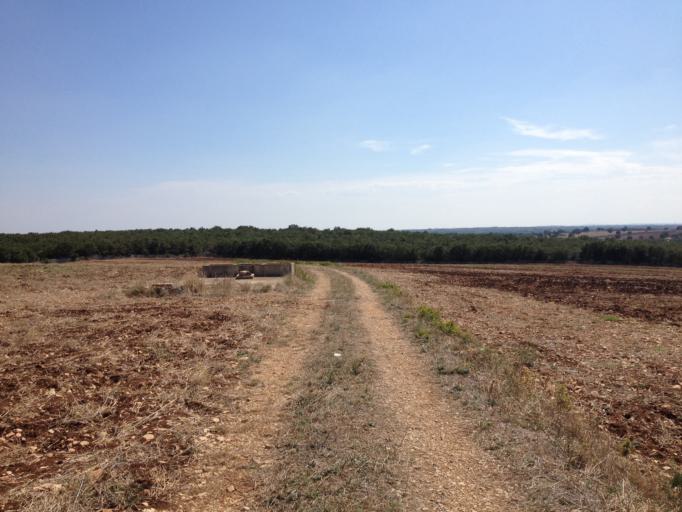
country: IT
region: Apulia
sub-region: Provincia di Bari
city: Gioia del Colle
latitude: 40.8230
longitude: 16.9979
